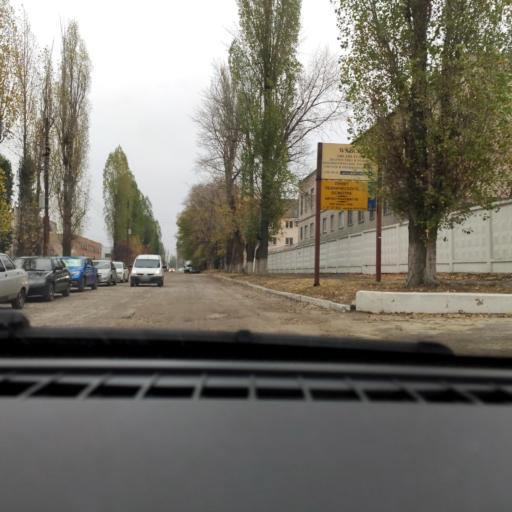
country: RU
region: Voronezj
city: Maslovka
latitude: 51.6473
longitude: 39.2928
